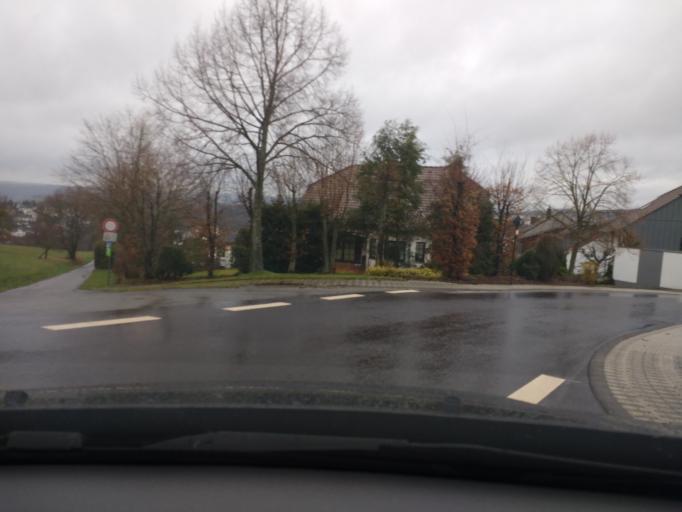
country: DE
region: Rheinland-Pfalz
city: Irsch
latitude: 49.7193
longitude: 6.6949
